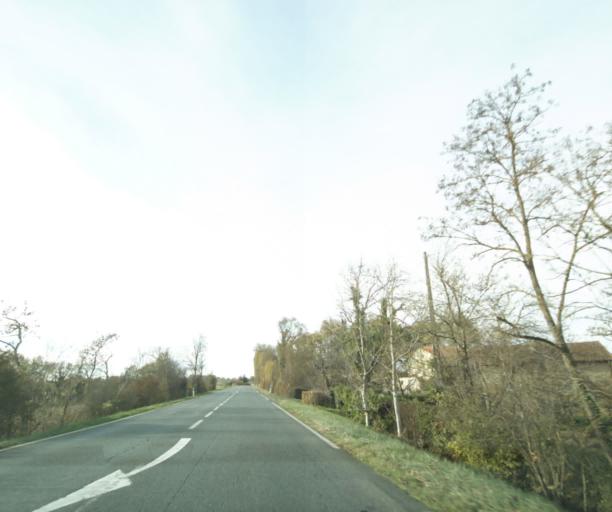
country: FR
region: Midi-Pyrenees
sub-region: Departement du Gers
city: Gimont
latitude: 43.6077
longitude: 0.9743
